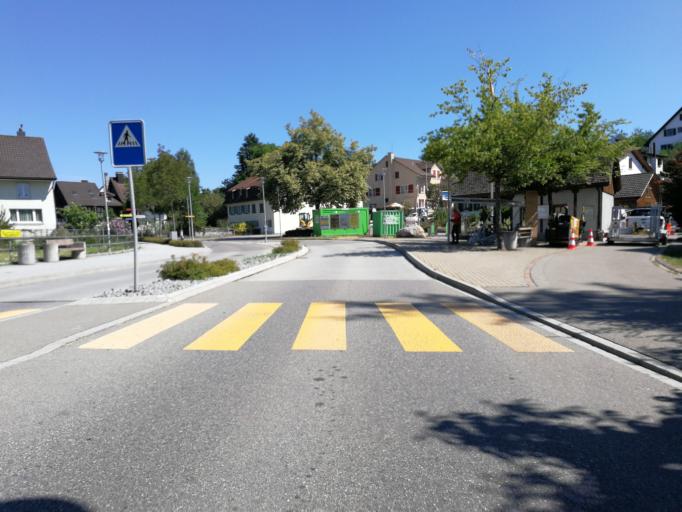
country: CH
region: Zurich
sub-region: Bezirk Hinwil
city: Gossau
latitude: 47.3202
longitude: 8.7575
